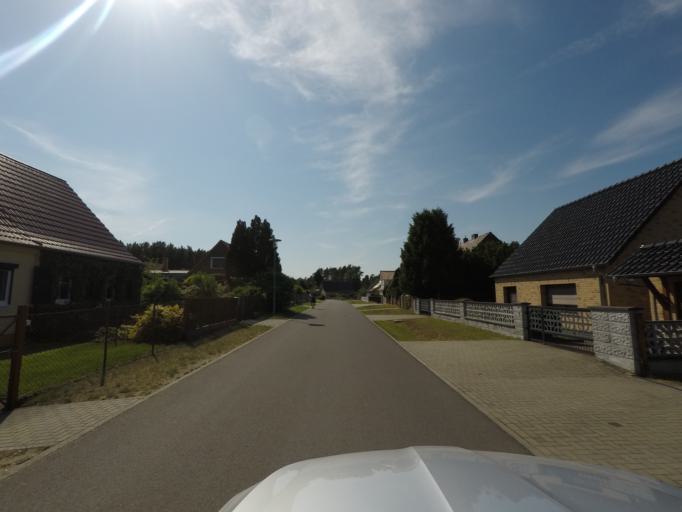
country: DE
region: Brandenburg
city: Melchow
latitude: 52.8610
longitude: 13.7189
